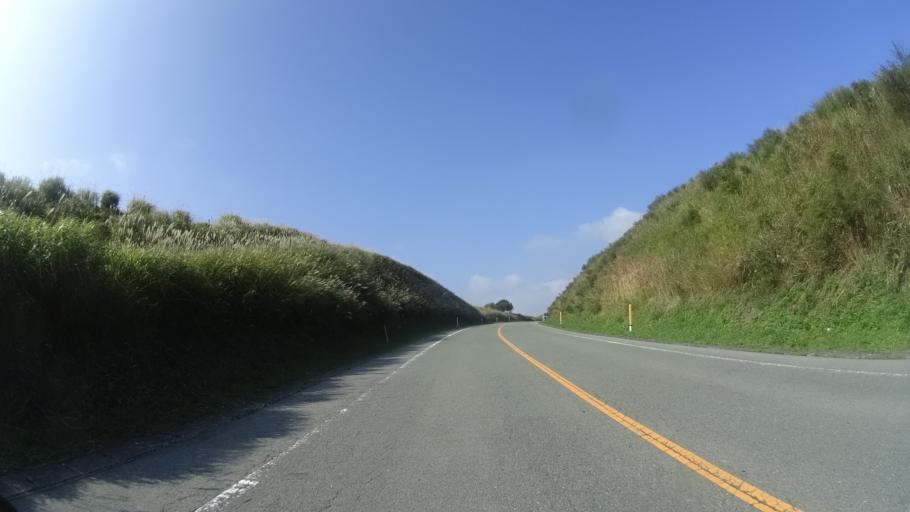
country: JP
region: Kumamoto
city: Aso
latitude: 33.0170
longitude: 131.0683
